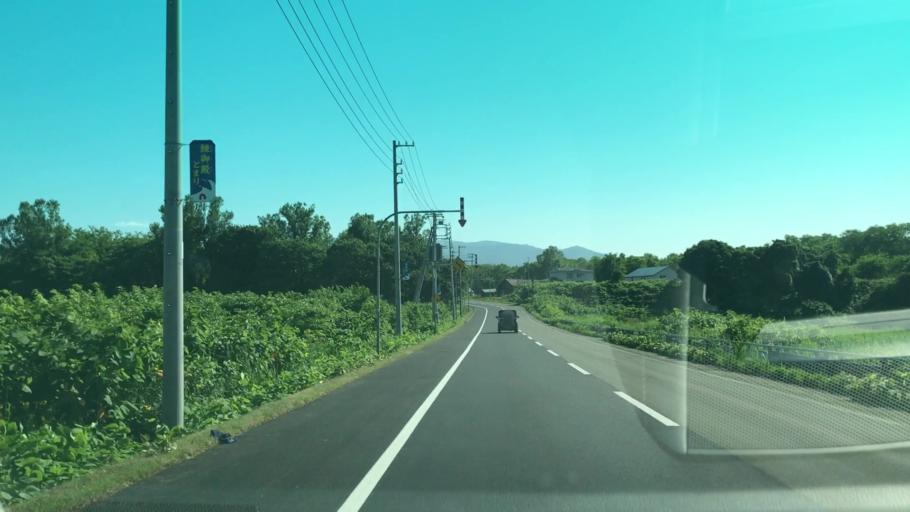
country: JP
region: Hokkaido
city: Iwanai
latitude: 43.0173
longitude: 140.5452
